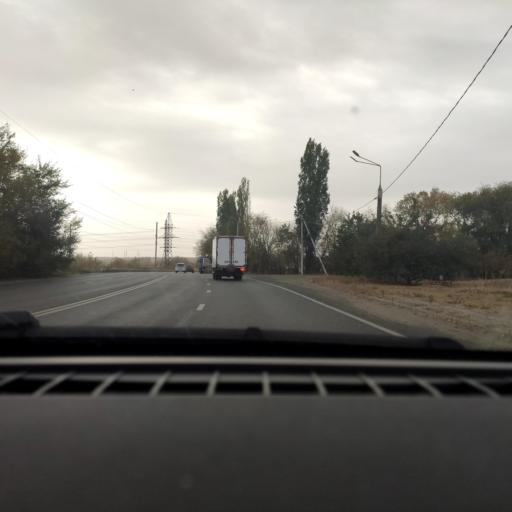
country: RU
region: Voronezj
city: Maslovka
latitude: 51.6303
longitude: 39.2866
